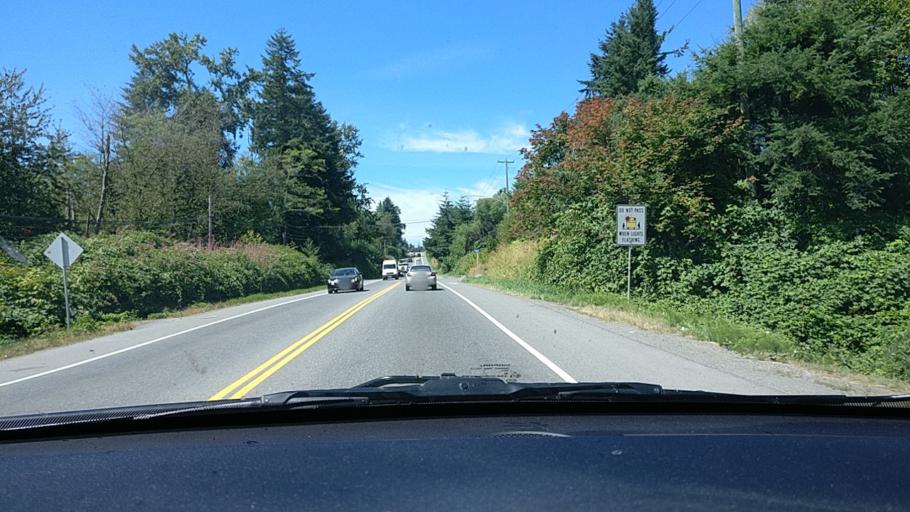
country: CA
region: British Columbia
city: Aldergrove
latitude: 49.0564
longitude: -122.3876
